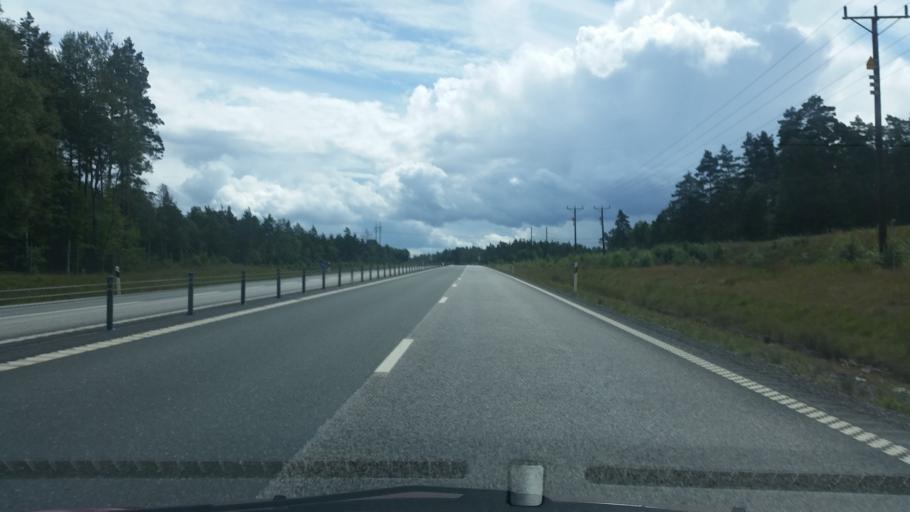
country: SE
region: Joenkoeping
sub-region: Gislaveds Kommun
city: Gislaved
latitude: 57.2988
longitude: 13.5851
